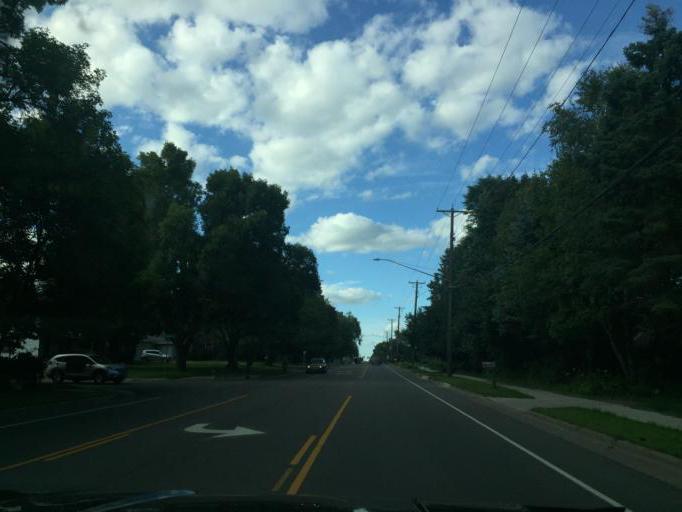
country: US
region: Minnesota
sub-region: Ramsey County
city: Roseville
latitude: 45.0025
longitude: -93.1463
